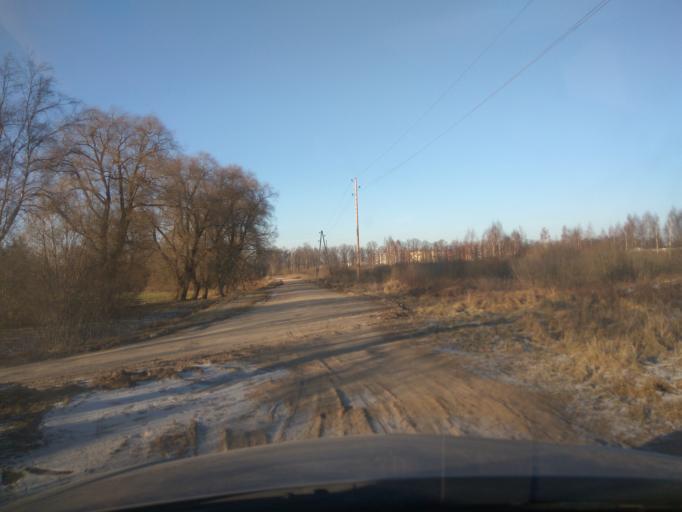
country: LV
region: Kuldigas Rajons
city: Kuldiga
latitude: 56.9629
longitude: 21.9585
